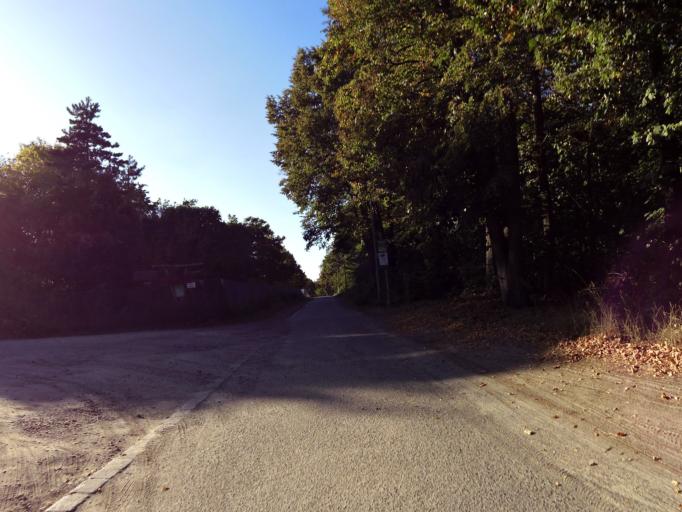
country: DE
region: Berlin
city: Grunewald
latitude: 52.4874
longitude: 13.2547
